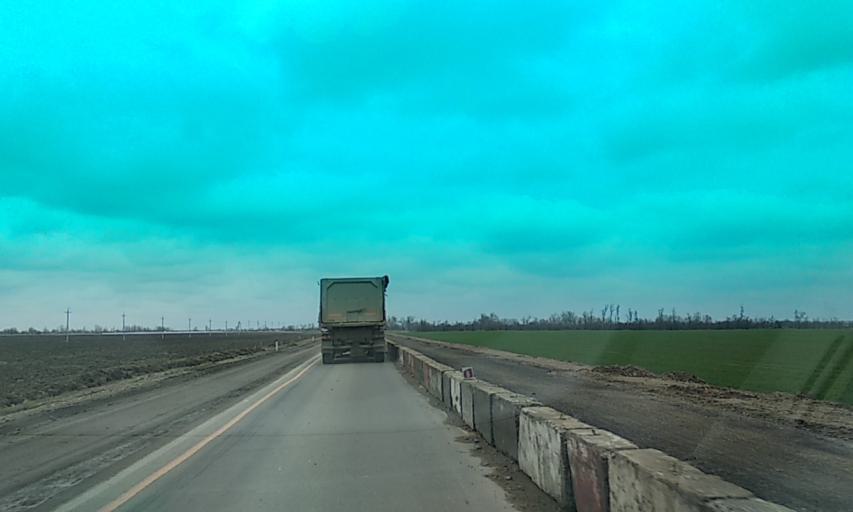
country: RU
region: Adygeya
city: Beloye
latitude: 45.0205
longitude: 39.6902
